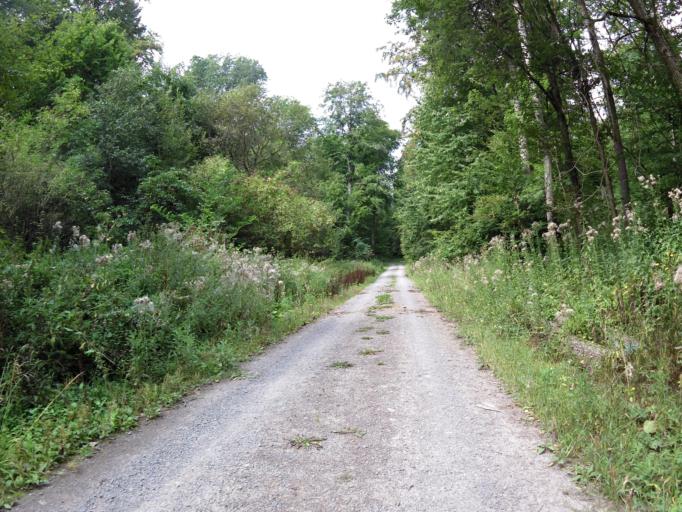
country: DE
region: Bavaria
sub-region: Regierungsbezirk Unterfranken
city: Kleinrinderfeld
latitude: 49.7191
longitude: 9.8362
